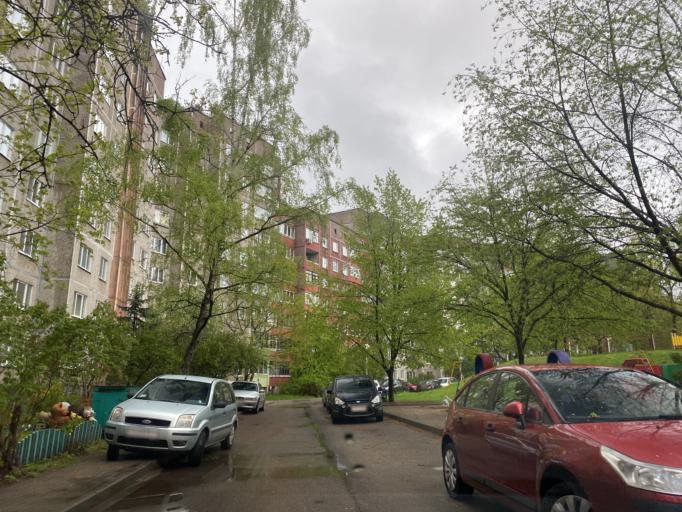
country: BY
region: Minsk
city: Bal'shavik
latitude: 53.9577
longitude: 27.6124
